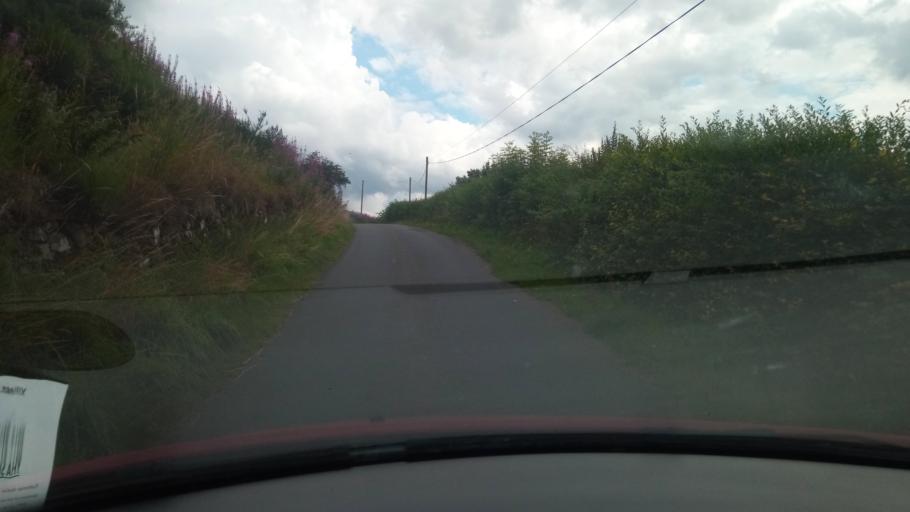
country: GB
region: Scotland
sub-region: The Scottish Borders
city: Jedburgh
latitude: 55.4116
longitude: -2.6229
